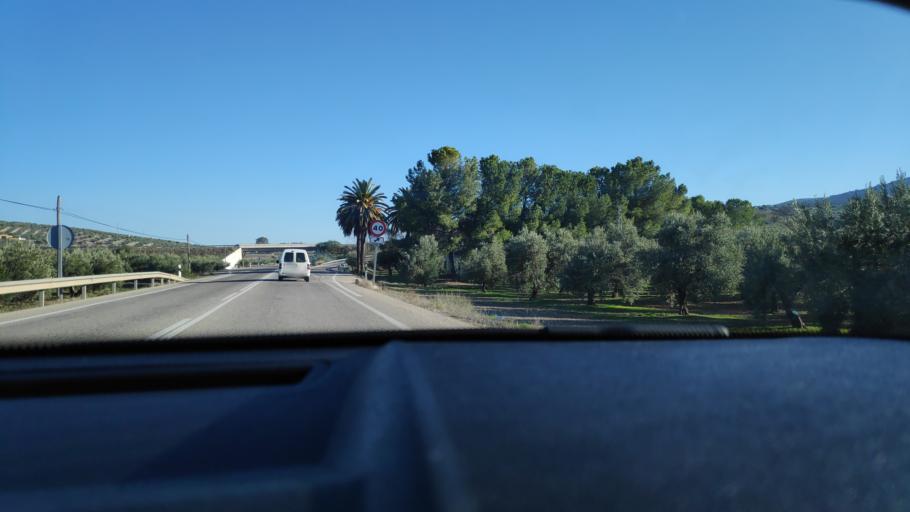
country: ES
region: Andalusia
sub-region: Province of Cordoba
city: Luque
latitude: 37.5775
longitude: -4.2749
